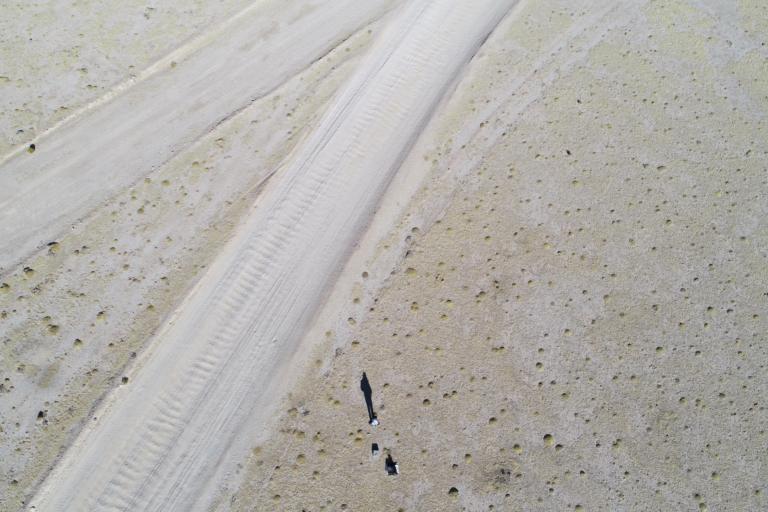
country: BO
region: Potosi
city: Colchani
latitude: -20.3578
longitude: -66.8841
